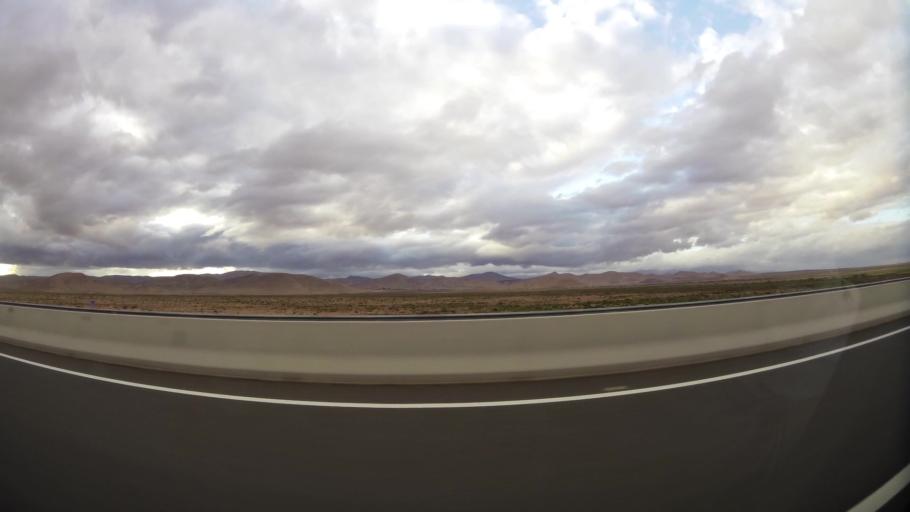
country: MA
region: Taza-Al Hoceima-Taounate
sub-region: Taza
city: Guercif
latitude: 34.3279
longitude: -3.5450
